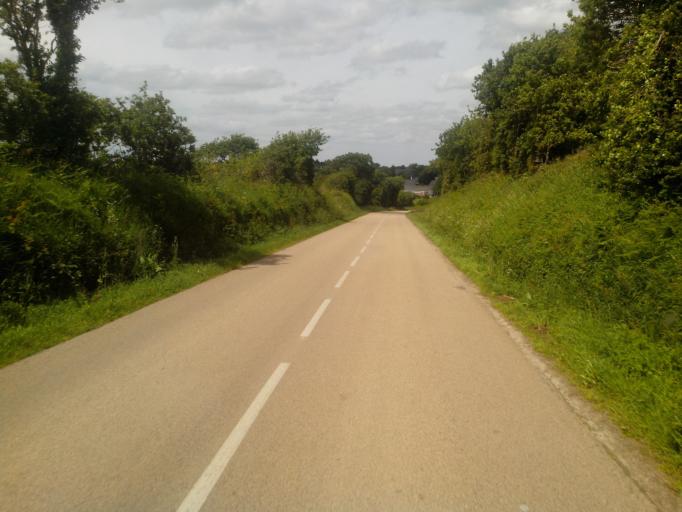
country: FR
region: Brittany
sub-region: Departement du Finistere
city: Guerlesquin
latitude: 48.5085
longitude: -3.6052
